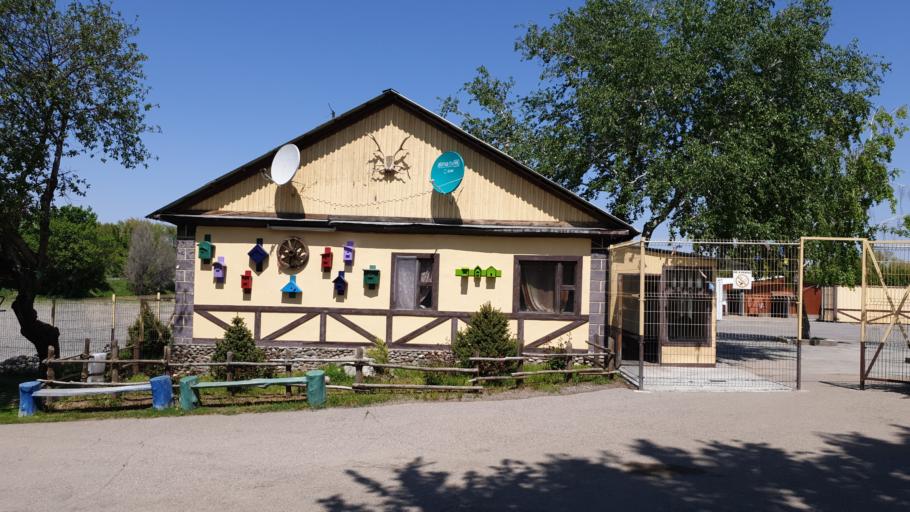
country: KZ
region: Almaty Oblysy
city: Esik
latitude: 43.4472
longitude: 77.4825
